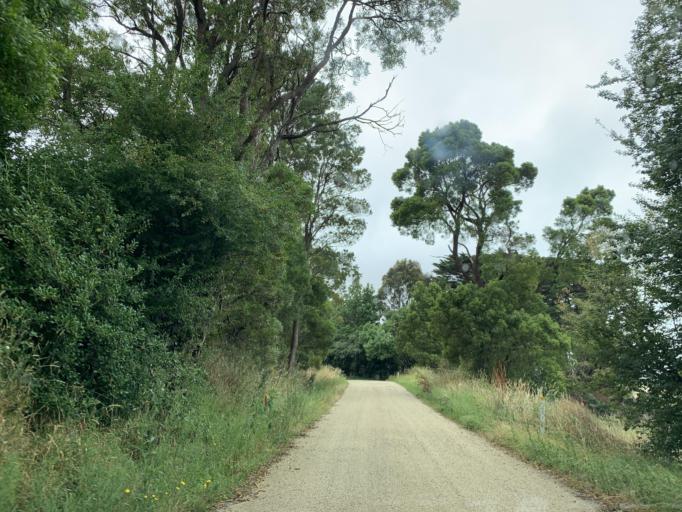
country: AU
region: Victoria
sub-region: Baw Baw
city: Warragul
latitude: -38.3485
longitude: 145.8684
